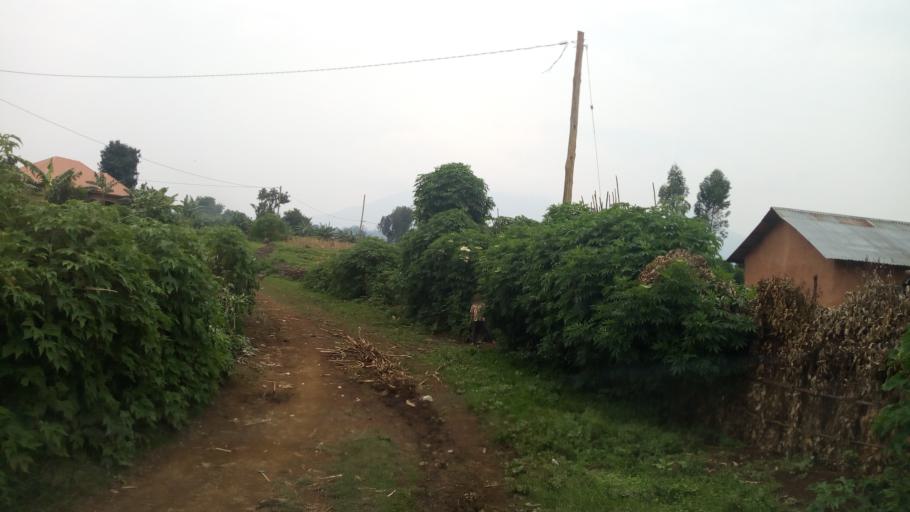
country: UG
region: Western Region
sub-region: Kisoro District
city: Kisoro
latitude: -1.2715
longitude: 29.6206
